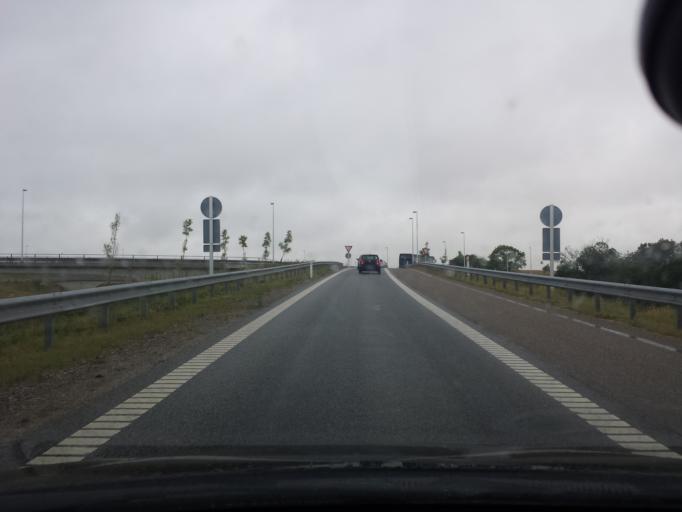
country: DK
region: South Denmark
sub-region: Sonderborg Kommune
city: Dybbol
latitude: 54.9234
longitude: 9.7277
